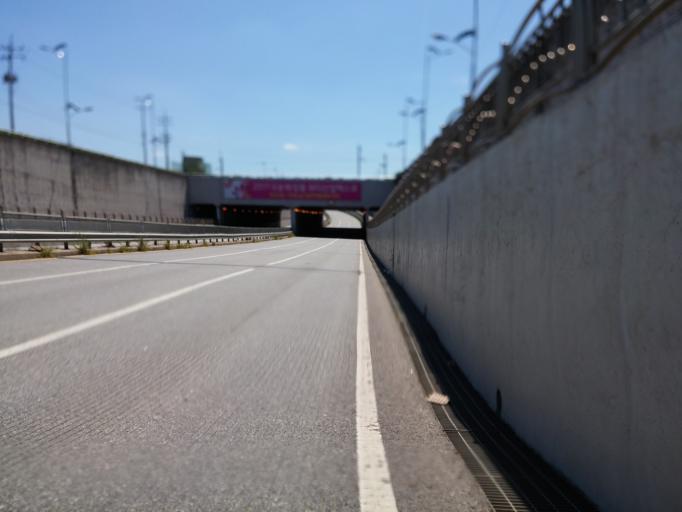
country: KR
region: Chungcheongbuk-do
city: Cheongju-si
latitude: 36.6258
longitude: 127.3371
